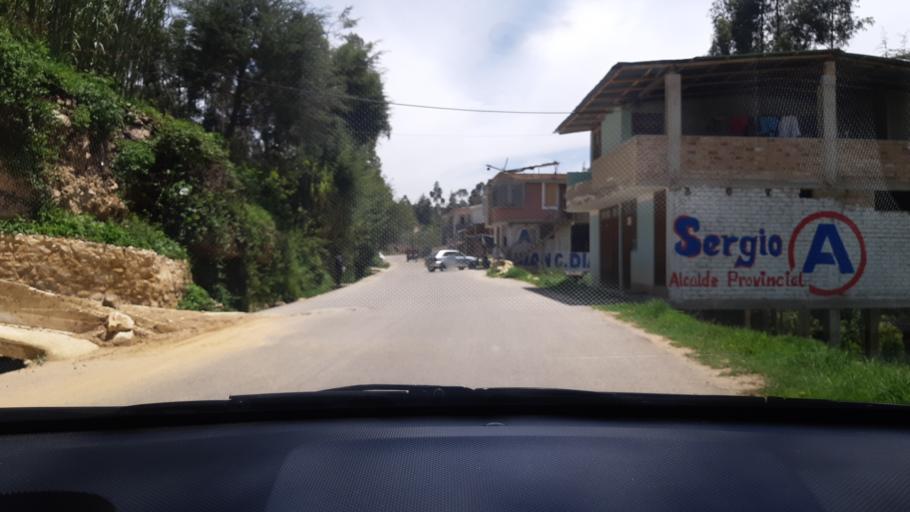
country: PE
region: Cajamarca
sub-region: Provincia de Cajamarca
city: Llacanora
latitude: -7.1857
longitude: -78.4412
